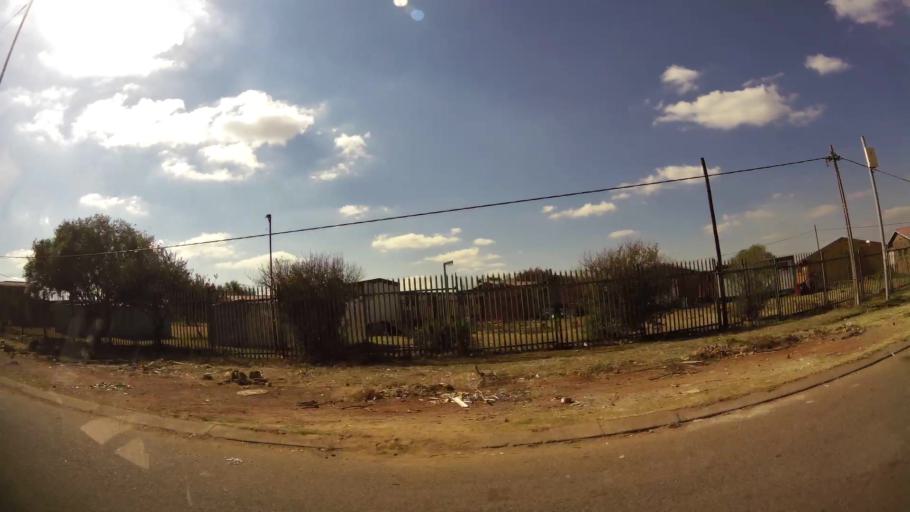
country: ZA
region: Gauteng
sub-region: West Rand District Municipality
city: Krugersdorp
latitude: -26.1650
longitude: 27.7833
